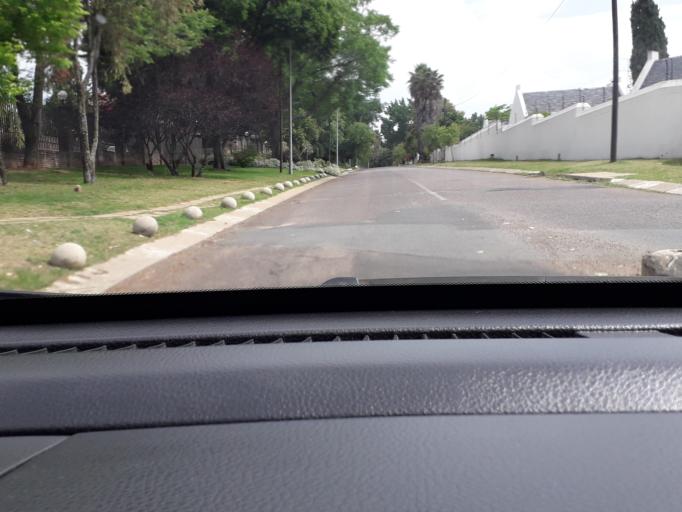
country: ZA
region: Gauteng
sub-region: City of Johannesburg Metropolitan Municipality
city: Modderfontein
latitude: -26.0952
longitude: 28.0720
